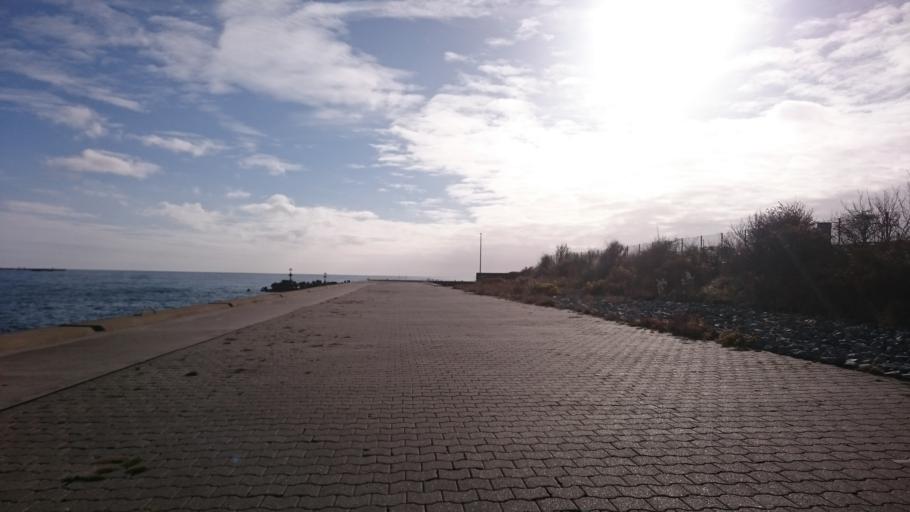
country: DE
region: Schleswig-Holstein
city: Helgoland
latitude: 54.1854
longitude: 7.8892
